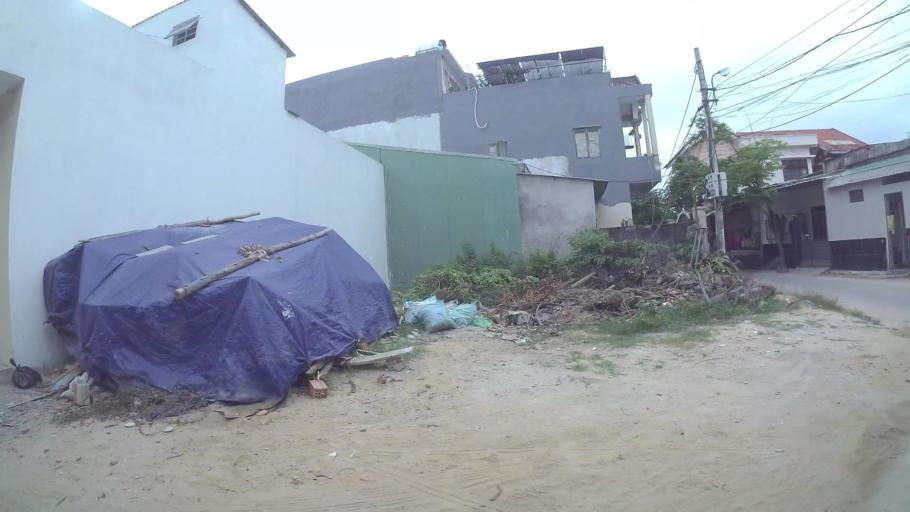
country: VN
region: Da Nang
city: Lien Chieu
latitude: 16.0627
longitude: 108.1679
